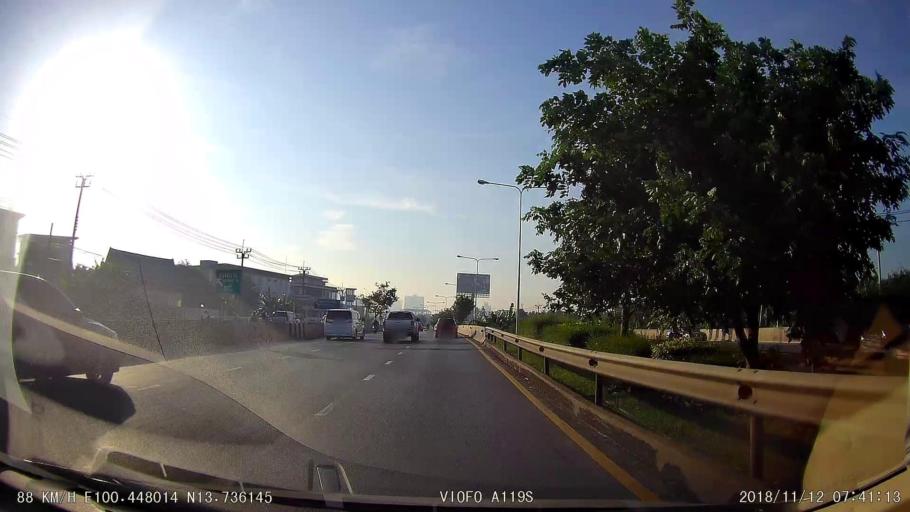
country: TH
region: Bangkok
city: Phasi Charoen
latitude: 13.7359
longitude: 100.4482
